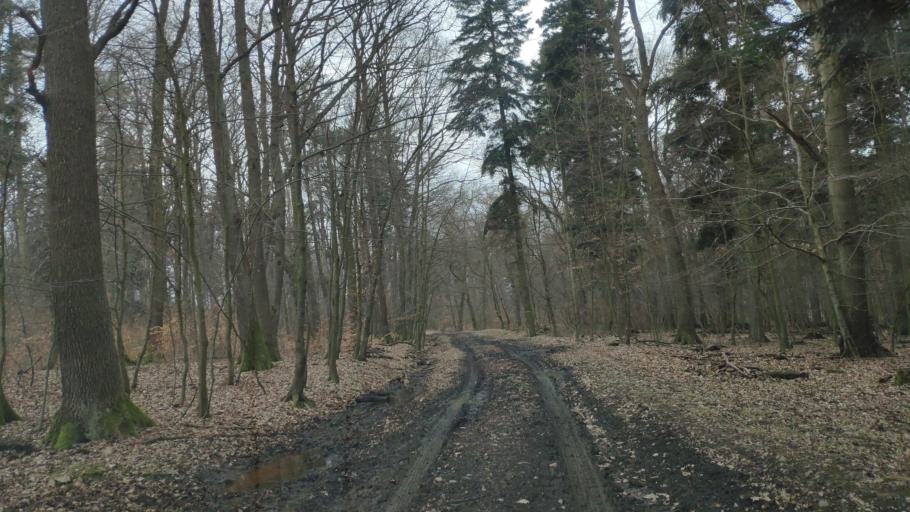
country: SK
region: Presovsky
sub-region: Okres Presov
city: Presov
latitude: 49.0722
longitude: 21.2788
